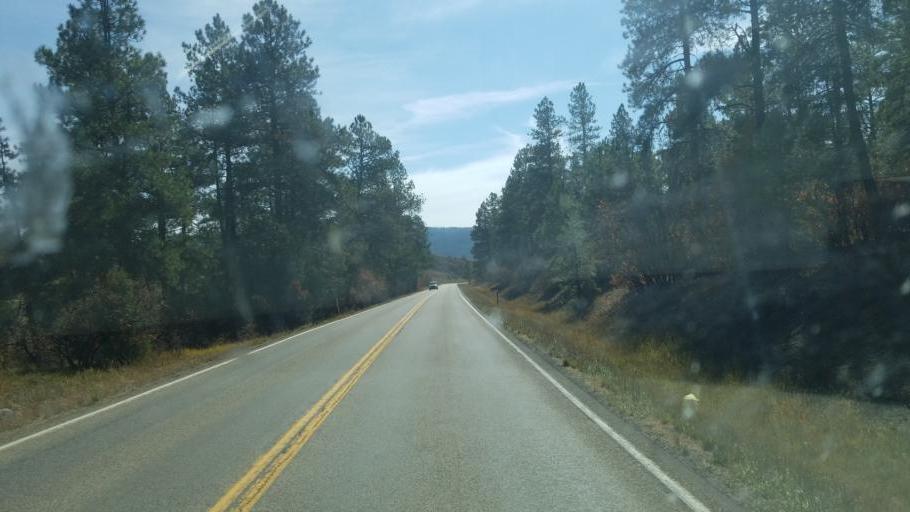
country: US
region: New Mexico
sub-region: Rio Arriba County
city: Dulce
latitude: 37.1011
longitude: -106.9141
